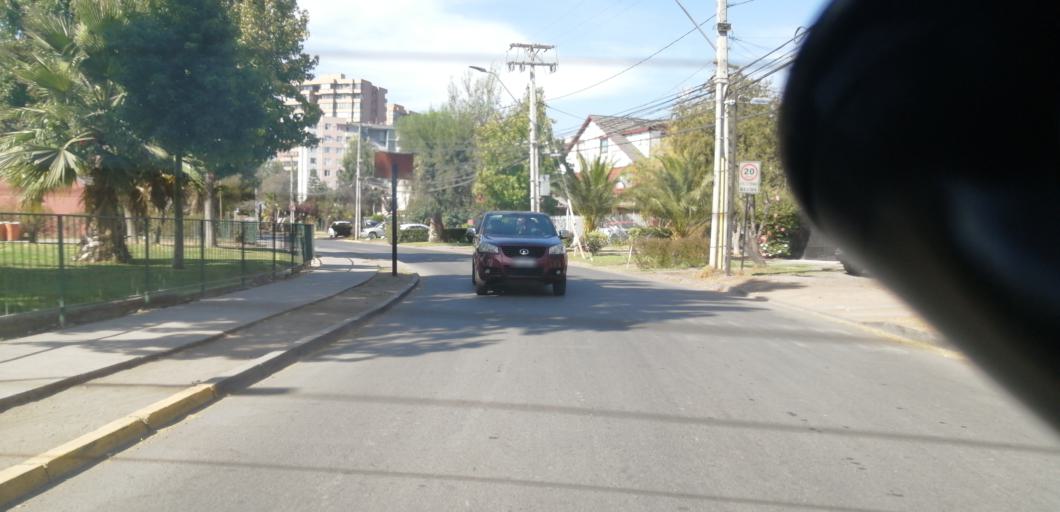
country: CL
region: Santiago Metropolitan
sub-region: Provincia de Santiago
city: Lo Prado
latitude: -33.4595
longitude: -70.7236
